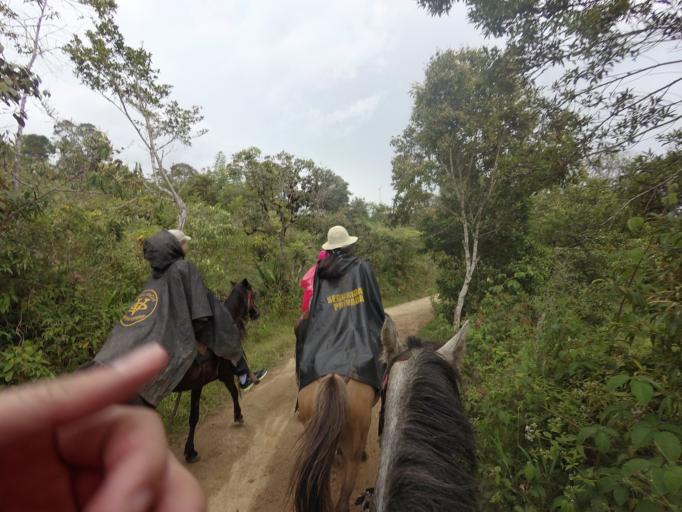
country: CO
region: Huila
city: San Agustin
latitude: 1.9027
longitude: -76.2927
